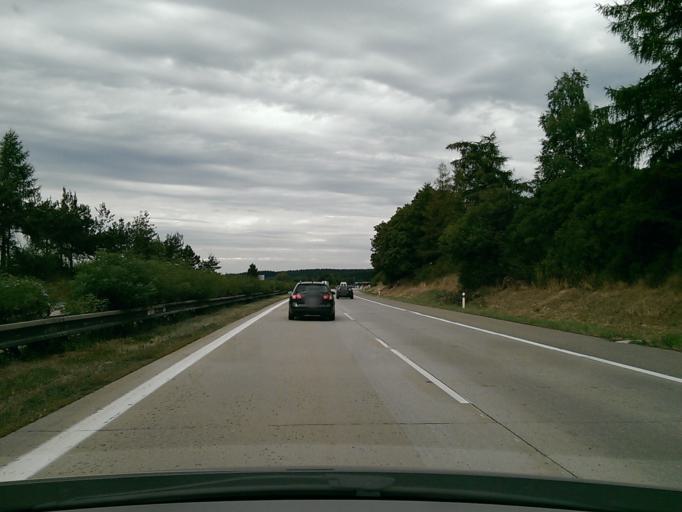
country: CZ
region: Vysocina
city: Luka nad Jihlavou
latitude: 49.4142
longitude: 15.7125
